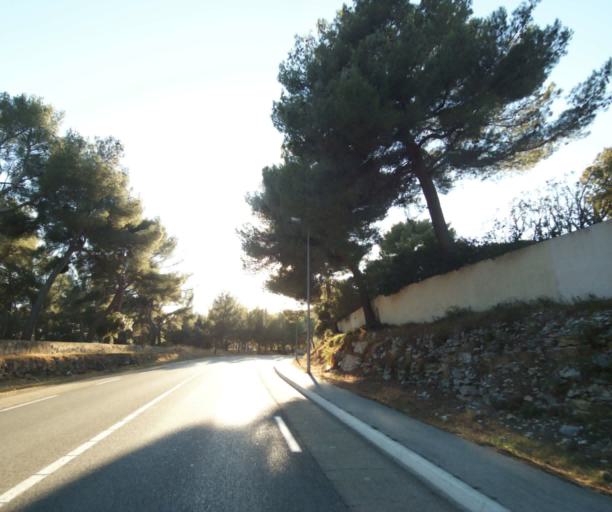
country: FR
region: Provence-Alpes-Cote d'Azur
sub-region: Departement des Bouches-du-Rhone
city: Cassis
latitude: 43.2307
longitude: 5.5423
